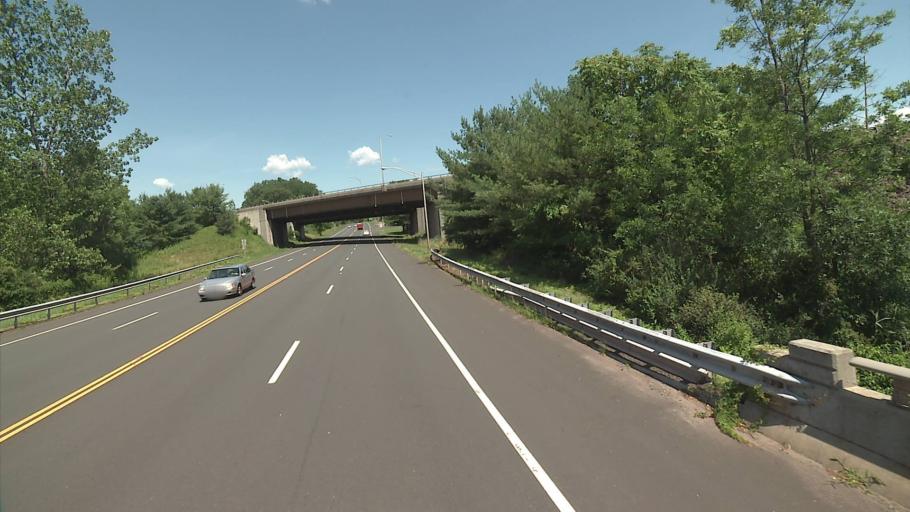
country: US
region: Connecticut
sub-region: Hartford County
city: Kensington
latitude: 41.6203
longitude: -72.7323
